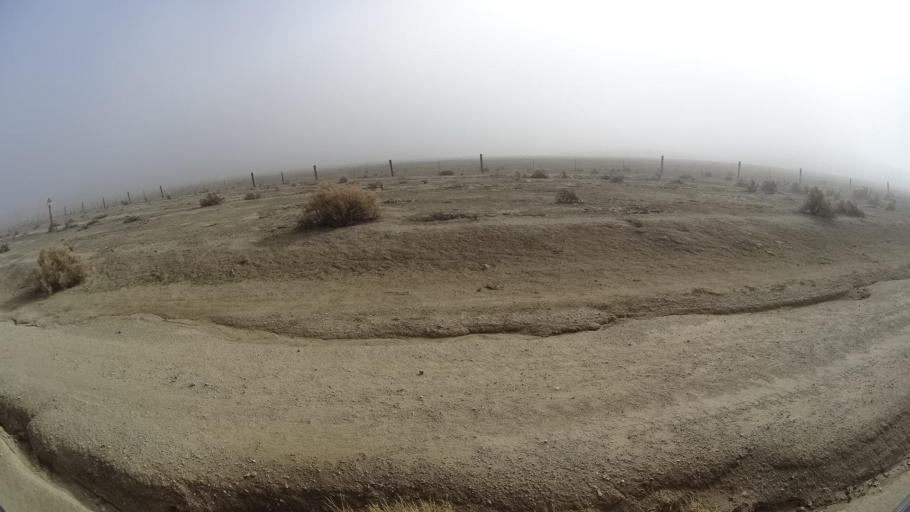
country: US
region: California
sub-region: Kern County
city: Maricopa
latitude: 35.0239
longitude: -119.4449
